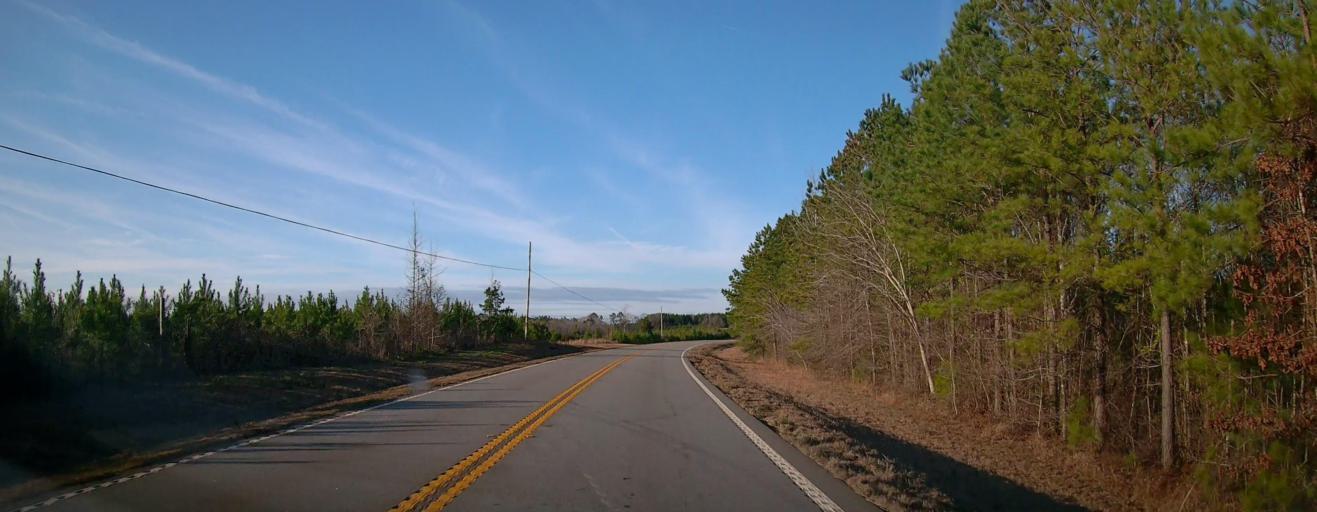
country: US
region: Alabama
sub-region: Chambers County
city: Valley
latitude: 32.7572
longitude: -85.0806
